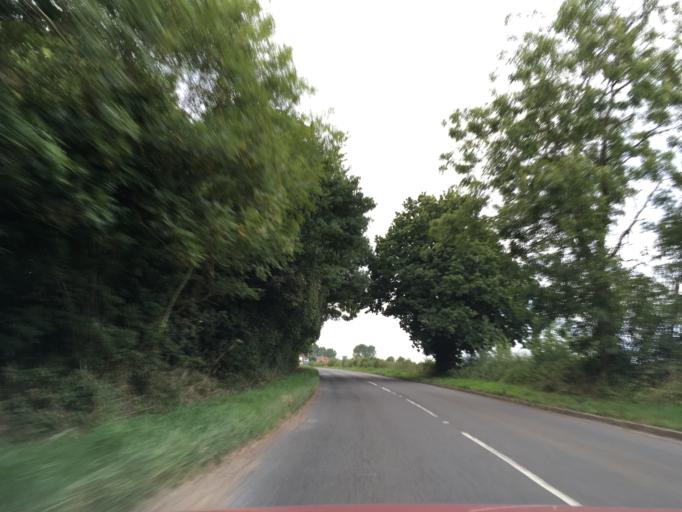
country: GB
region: England
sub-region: Wiltshire
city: Devizes
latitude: 51.3746
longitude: -2.0322
